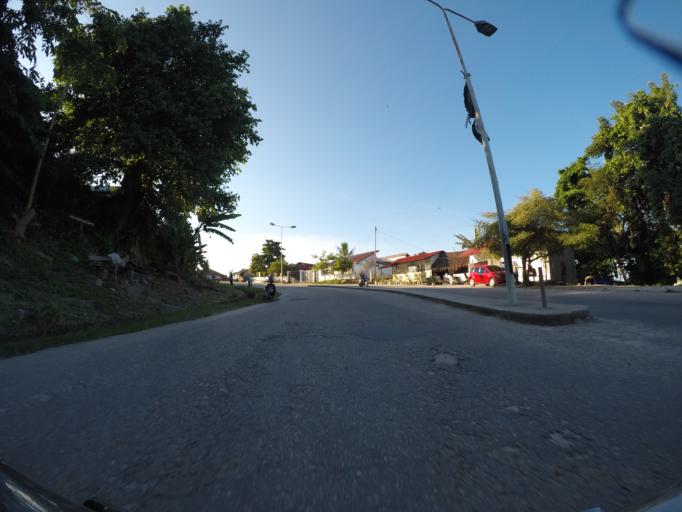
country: TZ
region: Pemba South
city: Uwelini
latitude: -5.3618
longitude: 39.6549
